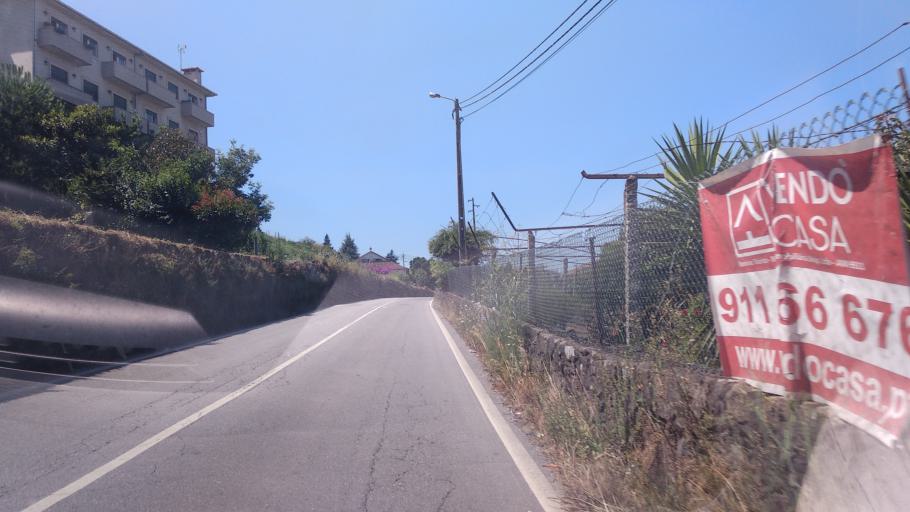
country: PT
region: Braga
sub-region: Braga
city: Adaufe
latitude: 41.5817
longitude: -8.4058
